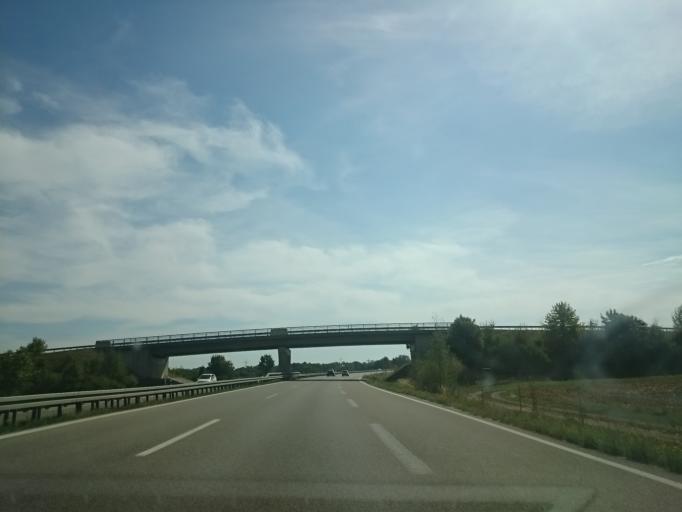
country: DE
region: Bavaria
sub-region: Swabia
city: Langweid
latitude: 48.5041
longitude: 10.8547
